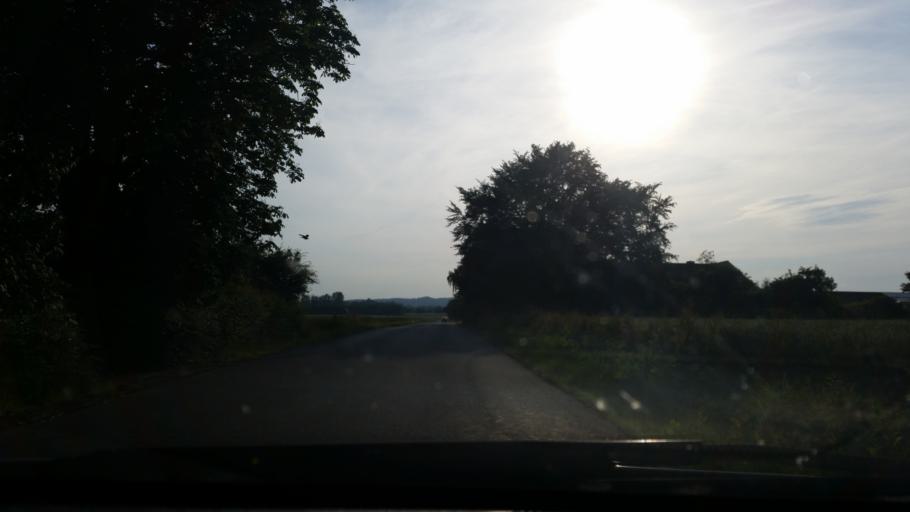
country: DK
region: Central Jutland
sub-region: Odder Kommune
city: Odder
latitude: 55.8908
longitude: 10.1565
